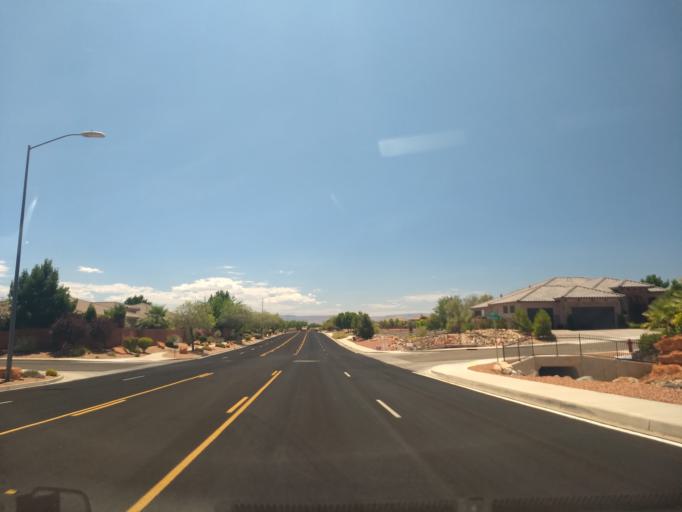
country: US
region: Utah
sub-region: Washington County
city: Washington
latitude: 37.1562
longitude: -113.5259
